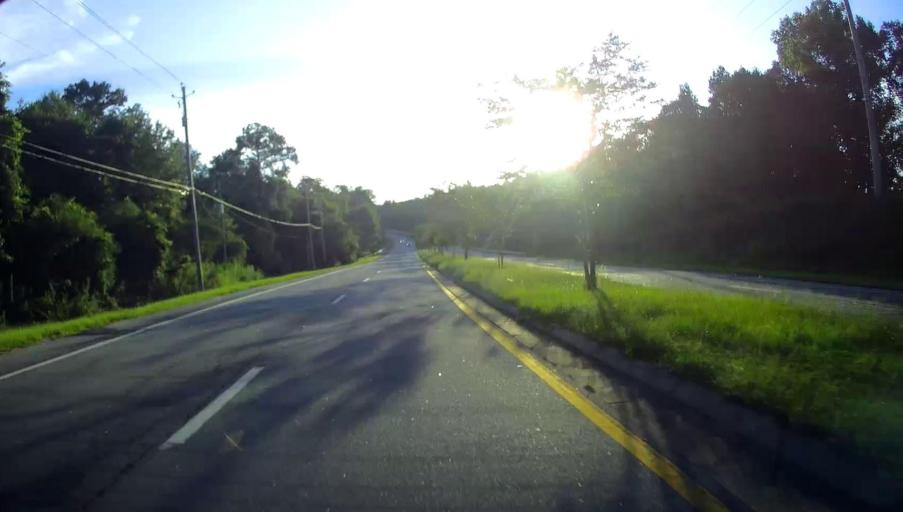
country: US
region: Georgia
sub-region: Muscogee County
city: Columbus
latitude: 32.5253
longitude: -84.8624
